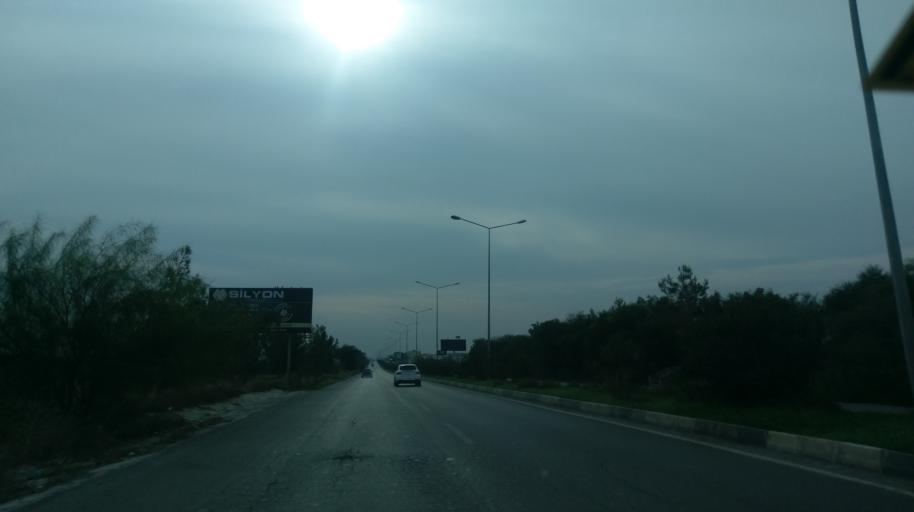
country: CY
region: Keryneia
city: Kyrenia
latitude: 35.2786
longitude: 33.2843
